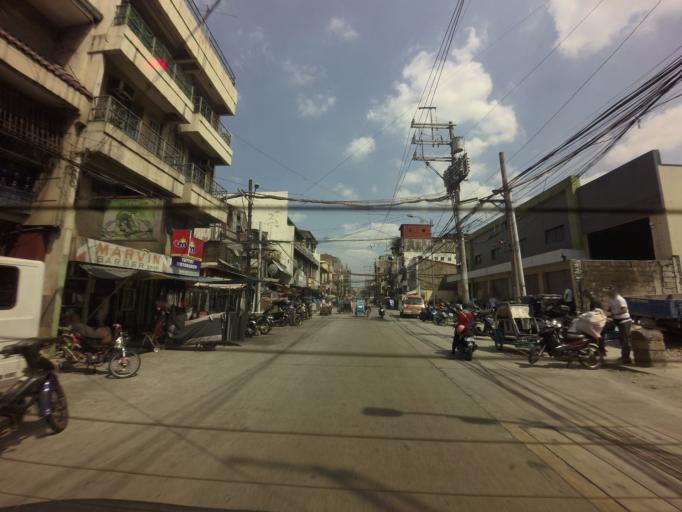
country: PH
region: Metro Manila
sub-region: City of Manila
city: Manila
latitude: 14.6109
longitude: 120.9682
